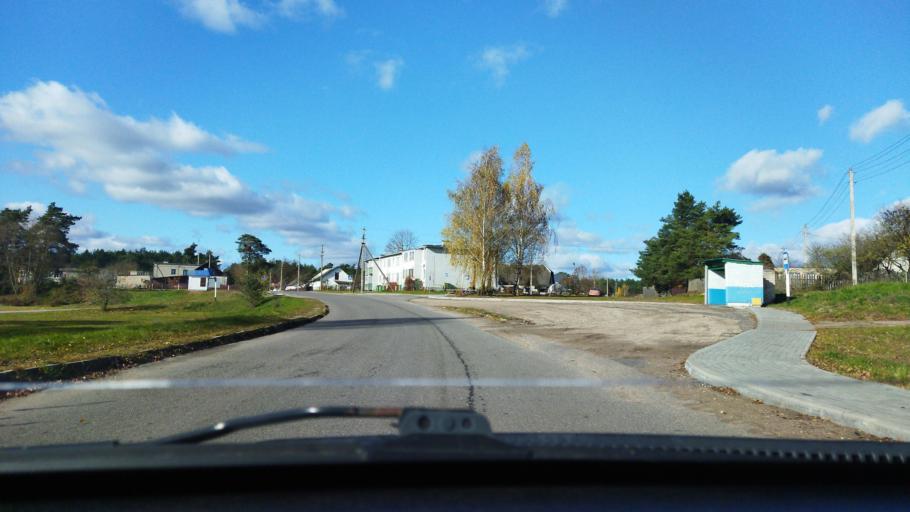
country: BY
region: Minsk
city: Svir
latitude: 54.8074
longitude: 26.2338
